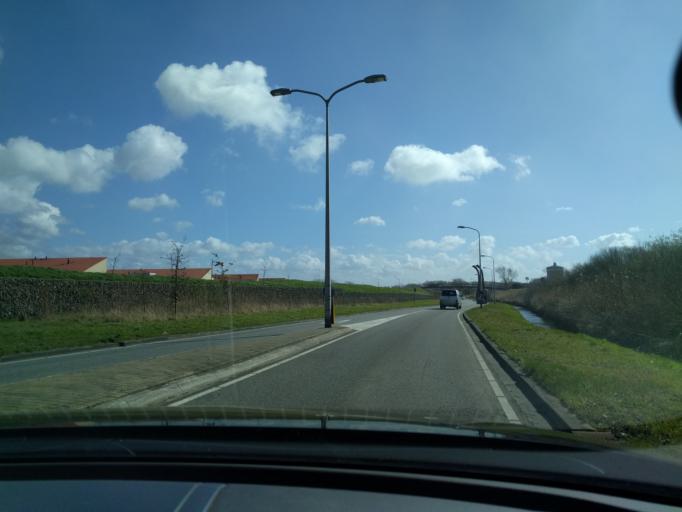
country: NL
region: South Holland
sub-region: Gemeente Katwijk
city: Katwijk aan den Rijn
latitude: 52.1931
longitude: 4.4091
